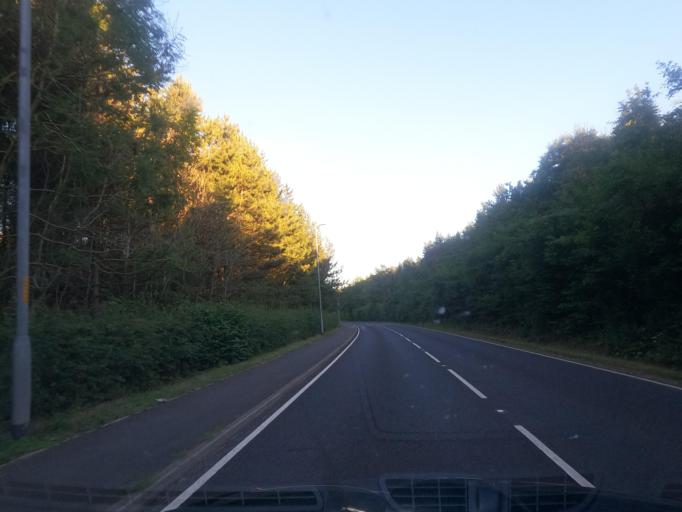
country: GB
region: England
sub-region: Northumberland
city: Seghill
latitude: 55.0790
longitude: -1.5486
